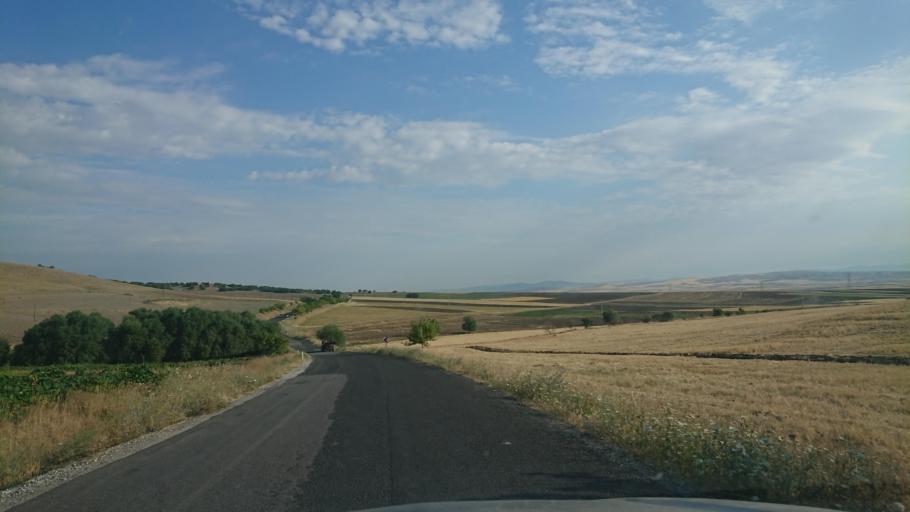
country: TR
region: Aksaray
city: Ortakoy
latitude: 38.7984
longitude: 34.0653
